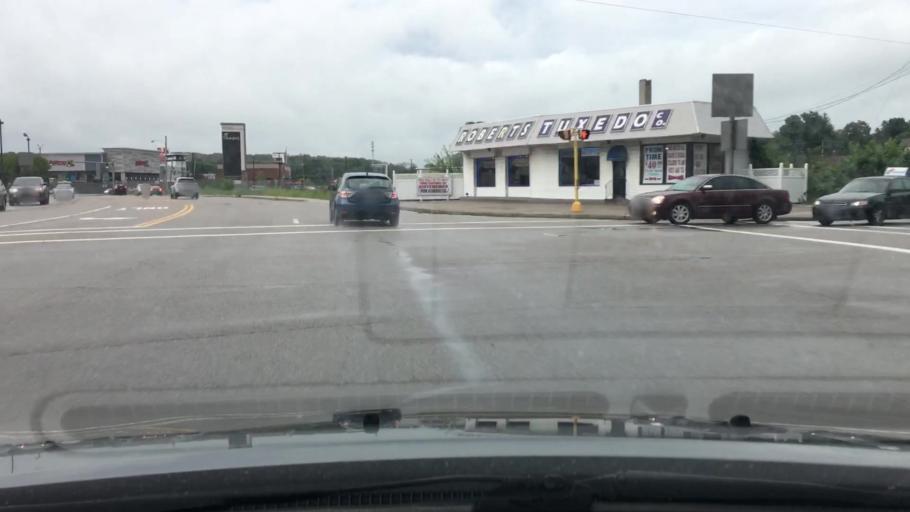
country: US
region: Rhode Island
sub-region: Providence County
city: Valley Falls
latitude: 41.9201
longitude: -71.3571
